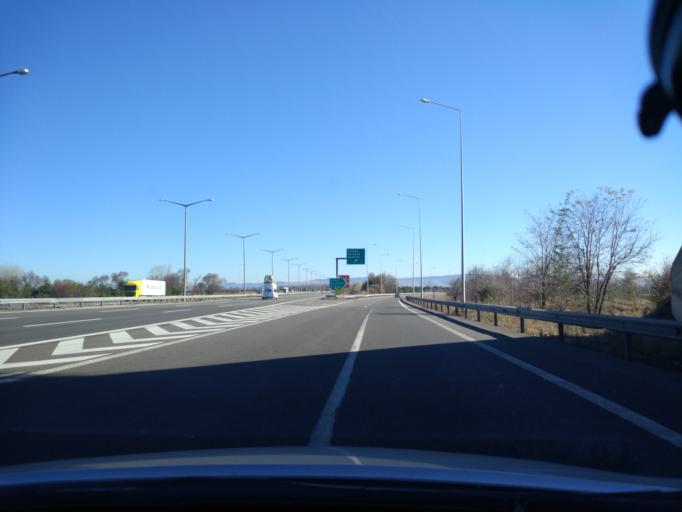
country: TR
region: Bolu
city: Gerede
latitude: 40.7395
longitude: 32.1793
